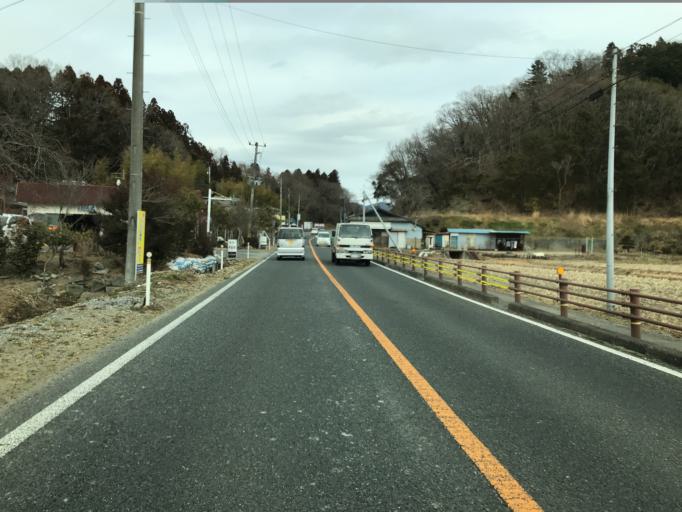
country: JP
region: Fukushima
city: Iwaki
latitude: 37.0918
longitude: 140.8731
